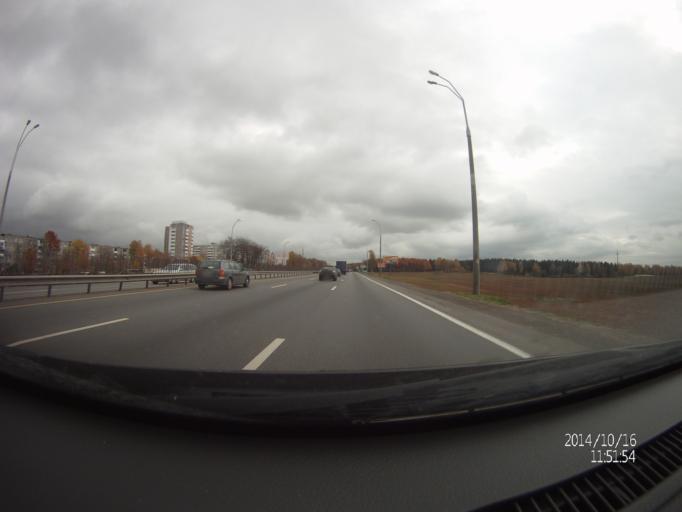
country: BY
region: Minsk
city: Hatava
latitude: 53.8335
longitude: 27.6329
